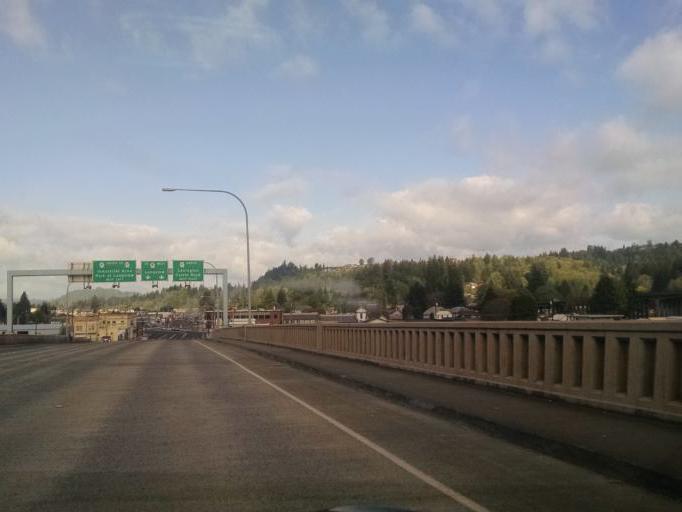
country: US
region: Washington
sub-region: Cowlitz County
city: Kelso
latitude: 46.1451
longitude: -122.9133
